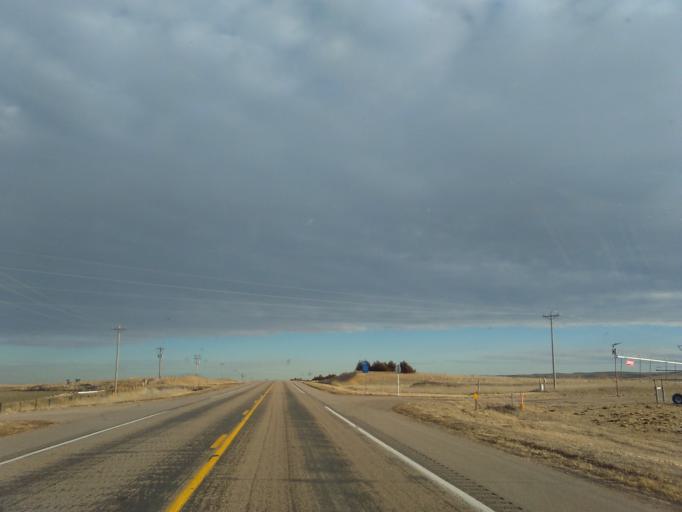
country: US
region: Nebraska
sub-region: Morrill County
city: Bridgeport
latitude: 41.6124
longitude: -103.0031
